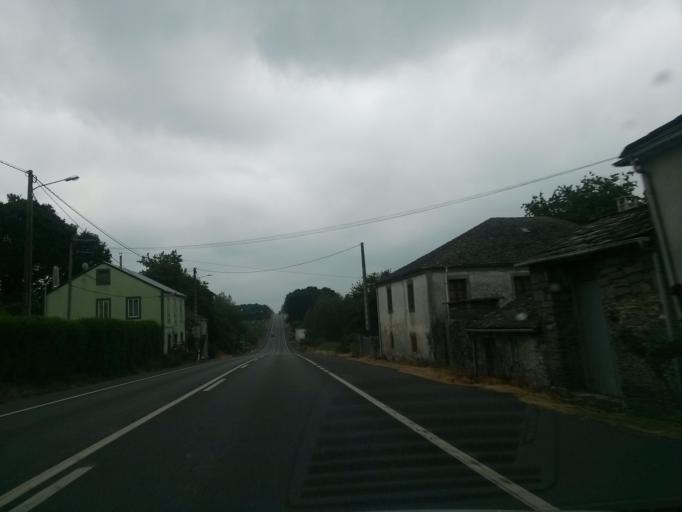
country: ES
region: Galicia
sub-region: Provincia de Lugo
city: Begonte
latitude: 43.1359
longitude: -7.6602
